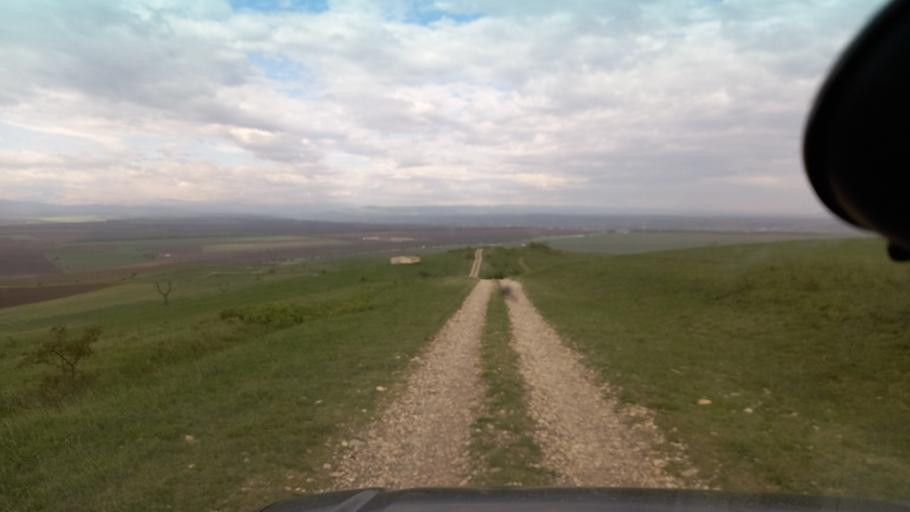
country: RU
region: Kabardino-Balkariya
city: Kuba-Taba
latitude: 43.8053
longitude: 43.4057
